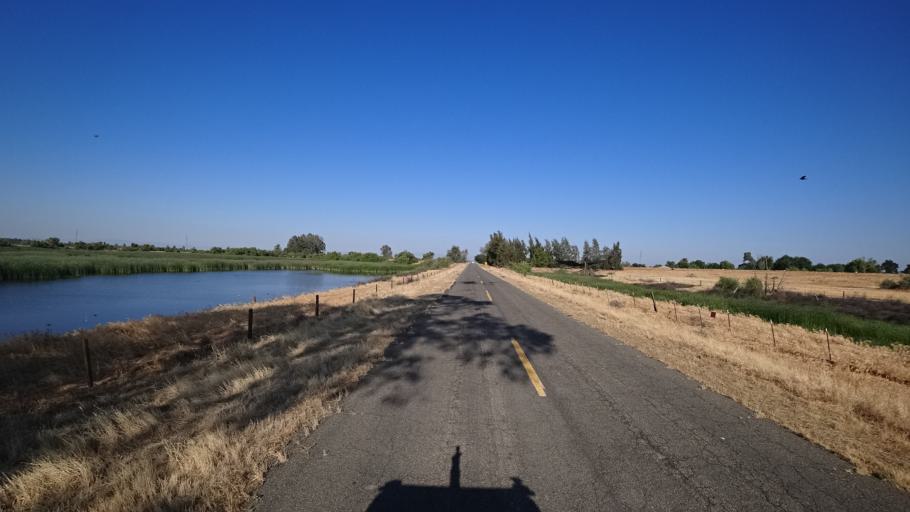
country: US
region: California
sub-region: Fresno County
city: Riverdale
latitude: 36.3766
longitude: -119.8810
